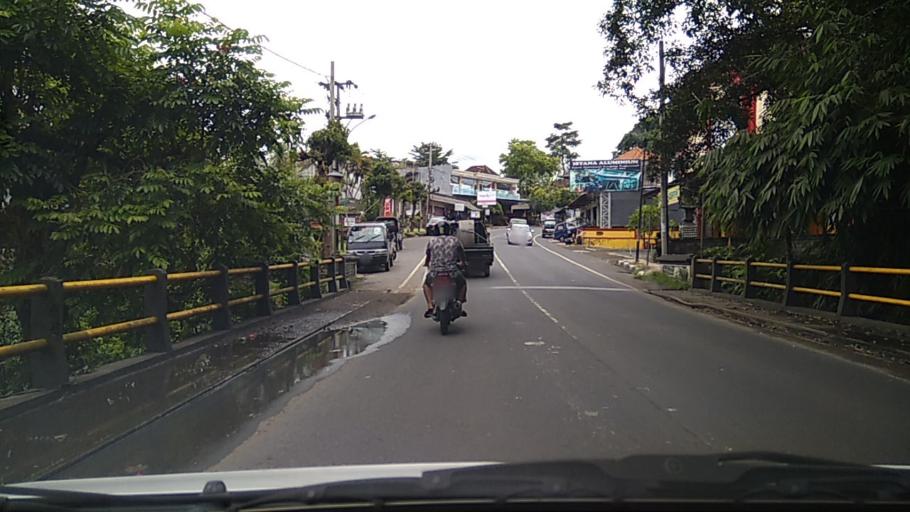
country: ID
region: Bali
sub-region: Kabupaten Gianyar
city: Ubud
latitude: -8.5352
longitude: 115.3106
